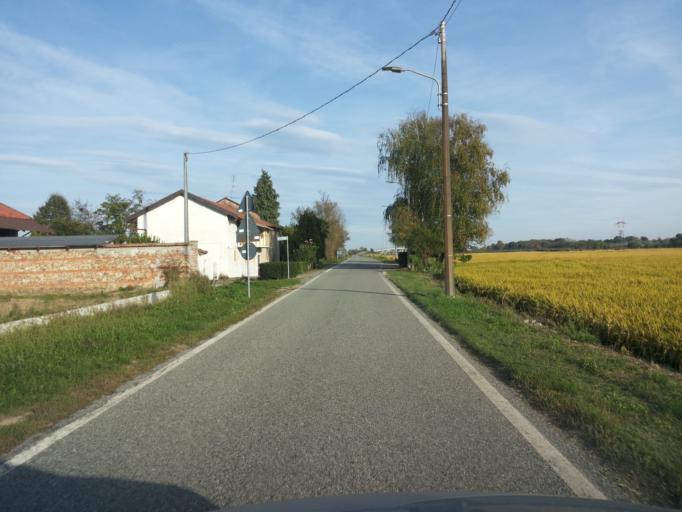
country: IT
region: Piedmont
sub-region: Provincia di Vercelli
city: Carisio
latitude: 45.4311
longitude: 8.1806
